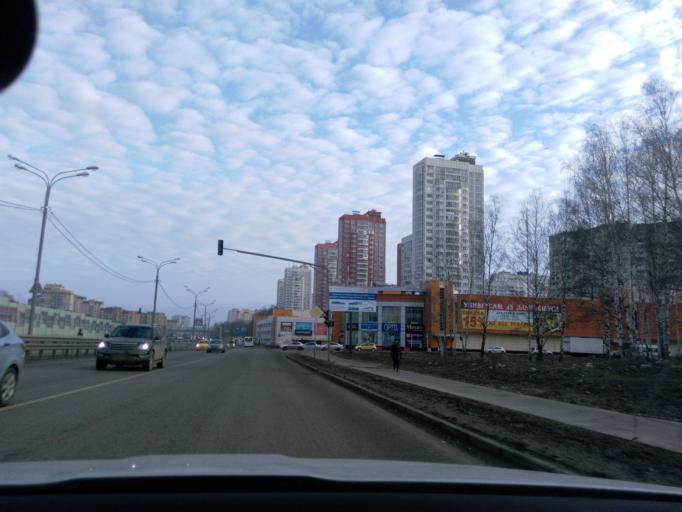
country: RU
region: Moskovskaya
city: Dolgoprudnyy
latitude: 55.9298
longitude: 37.4932
